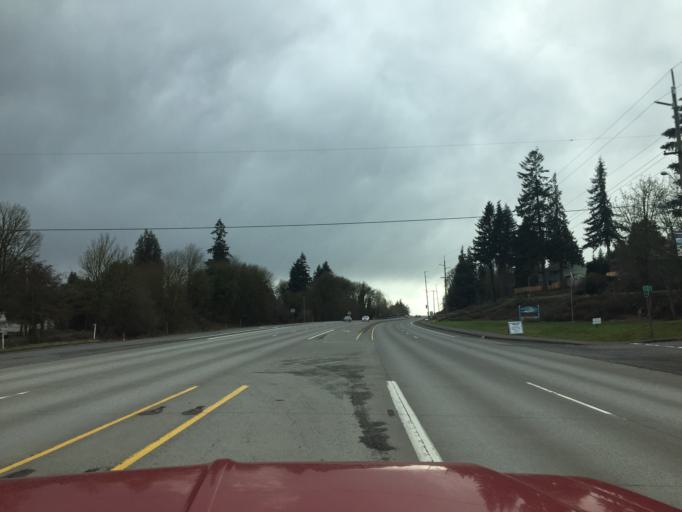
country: US
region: Oregon
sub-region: Columbia County
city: Columbia City
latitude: 45.8895
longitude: -122.8114
